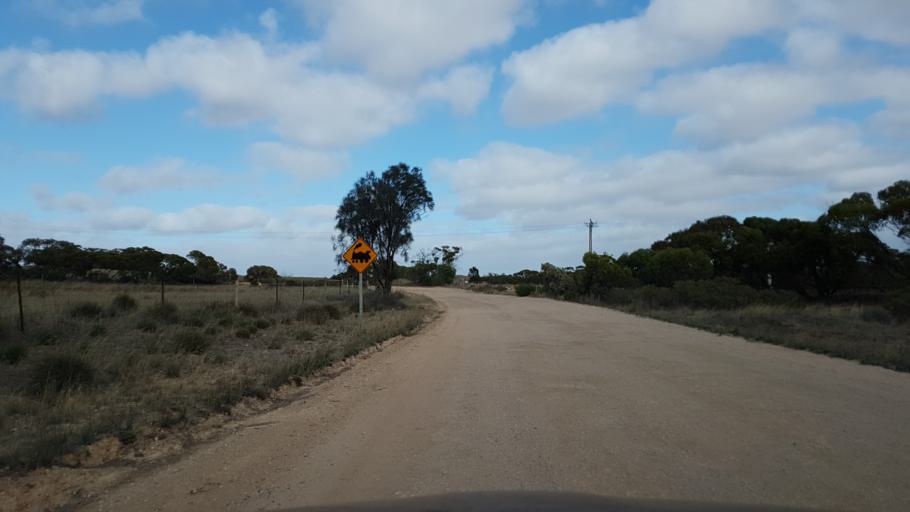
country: AU
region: South Australia
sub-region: Murray Bridge
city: Murray Bridge
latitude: -35.1110
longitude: 139.2001
